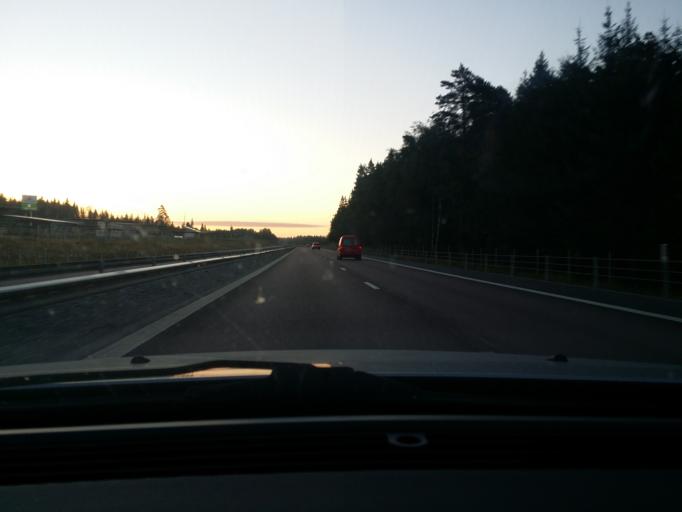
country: SE
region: Vaestmanland
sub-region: Vasteras
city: Tillberga
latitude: 59.6247
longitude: 16.7538
